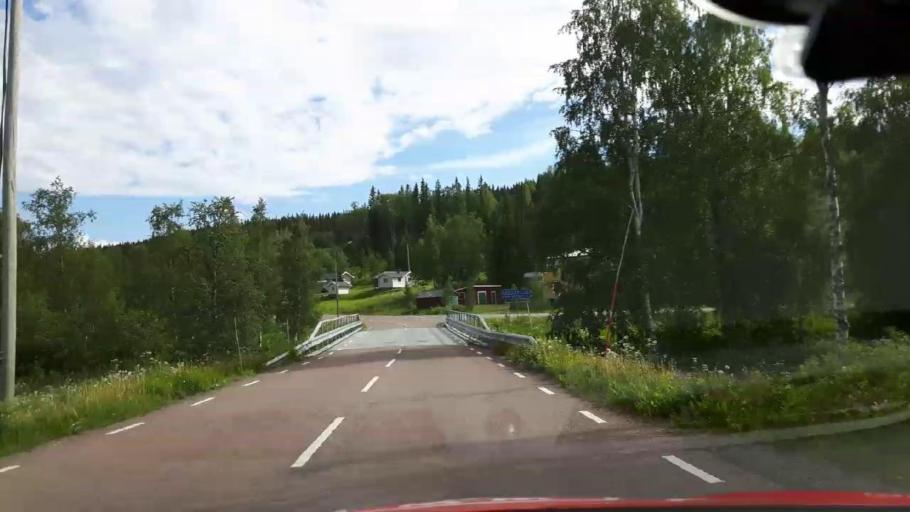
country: SE
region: Jaemtland
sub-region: Krokoms Kommun
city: Valla
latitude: 63.9045
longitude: 14.2130
